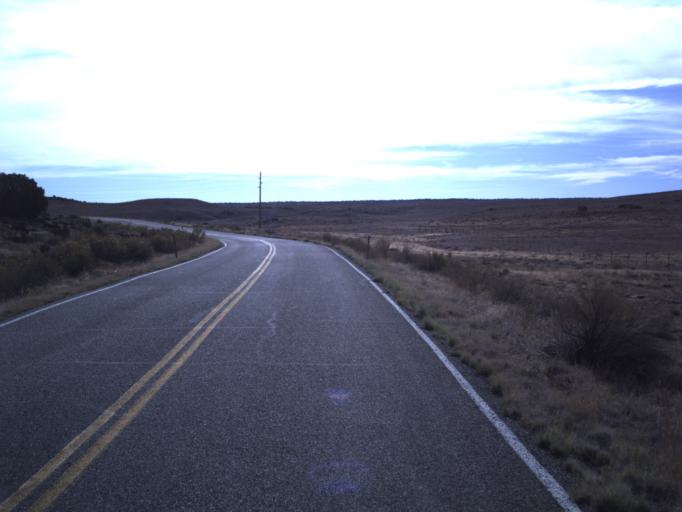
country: US
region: Utah
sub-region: San Juan County
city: Blanding
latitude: 37.4185
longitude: -109.4344
